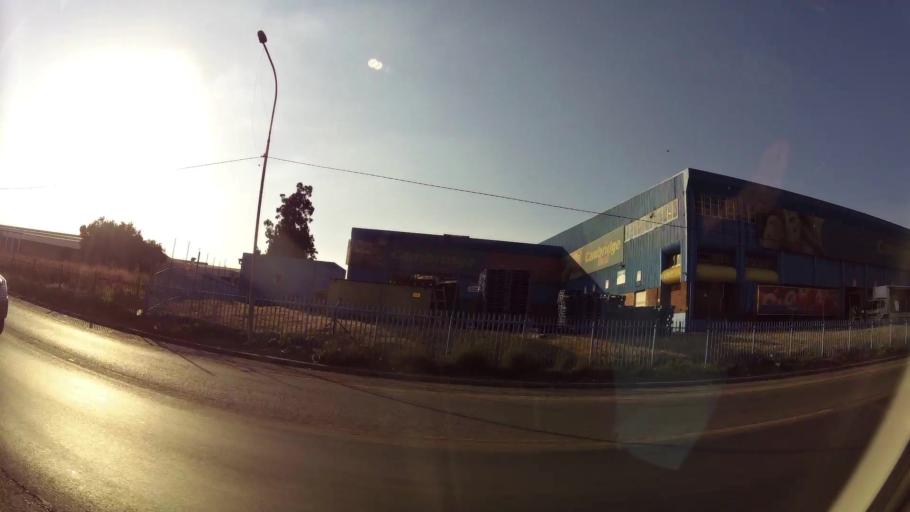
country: ZA
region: Gauteng
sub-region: City of Johannesburg Metropolitan Municipality
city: Johannesburg
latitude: -26.2118
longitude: 28.0958
